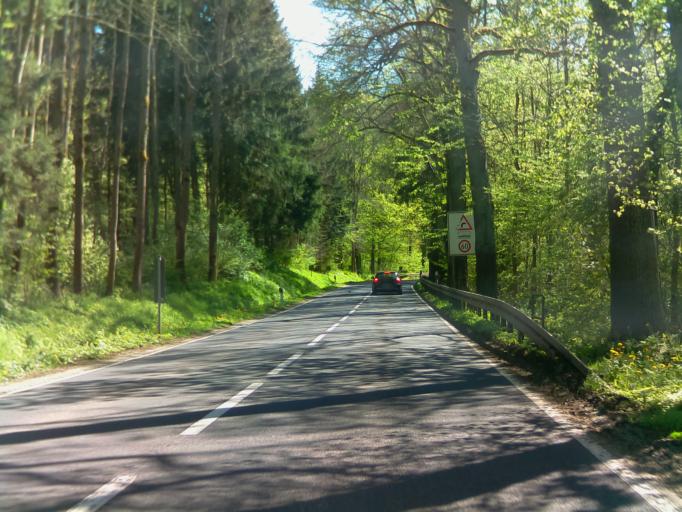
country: DE
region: Hesse
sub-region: Regierungsbezirk Giessen
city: Lauterbach
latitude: 50.5989
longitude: 9.3912
